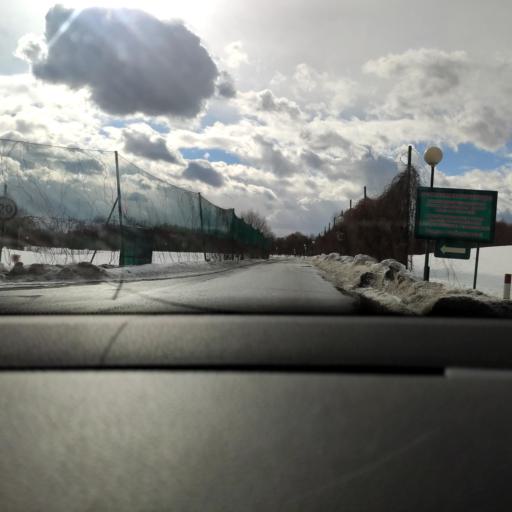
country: RU
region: Moskovskaya
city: Fili
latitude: 55.7597
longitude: 37.4549
